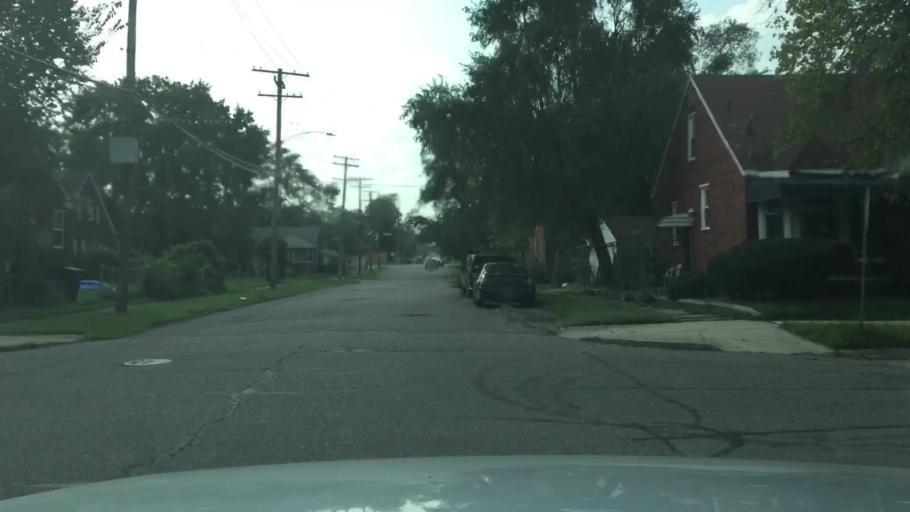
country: US
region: Michigan
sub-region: Wayne County
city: Dearborn
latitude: 42.3606
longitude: -83.1948
